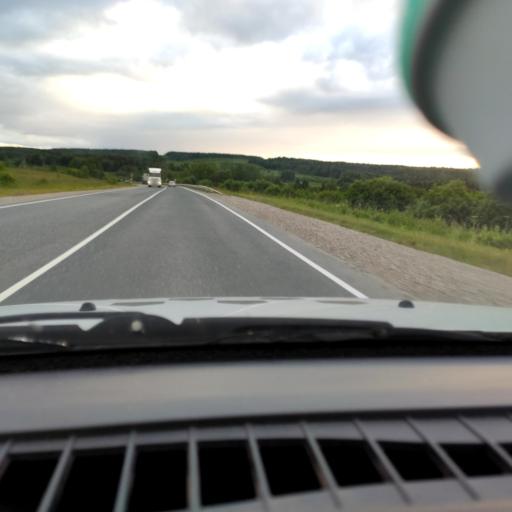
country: RU
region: Perm
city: Kalino
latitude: 58.2863
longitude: 57.4214
